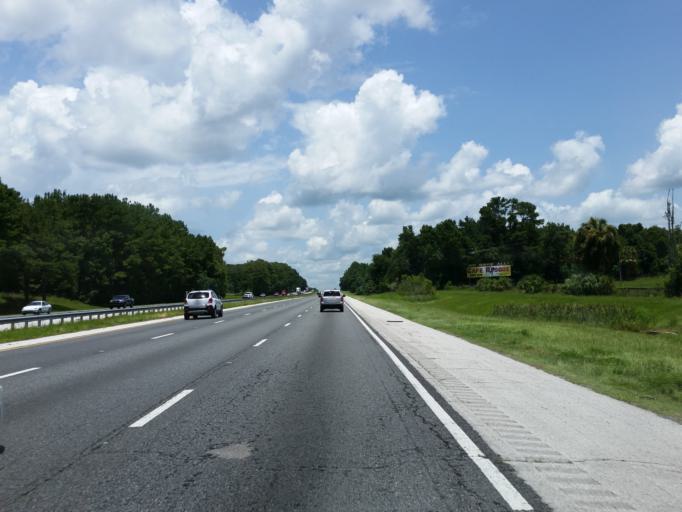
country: US
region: Florida
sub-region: Marion County
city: Citra
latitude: 29.3683
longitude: -82.2269
